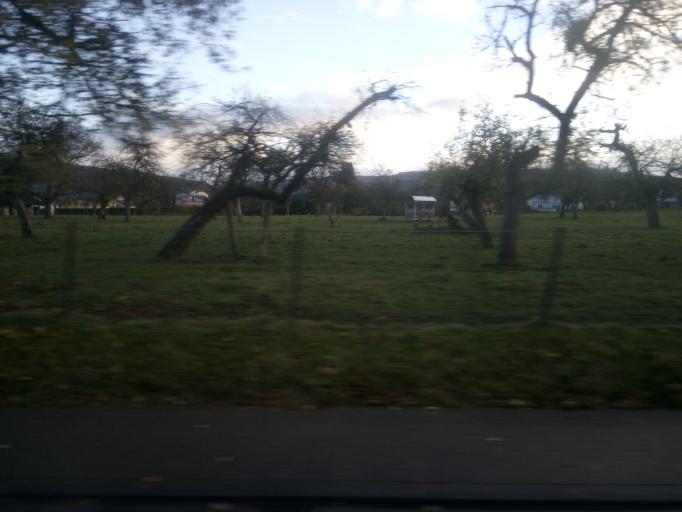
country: DE
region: Rheinland-Pfalz
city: Gentingen
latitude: 49.9167
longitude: 6.2251
